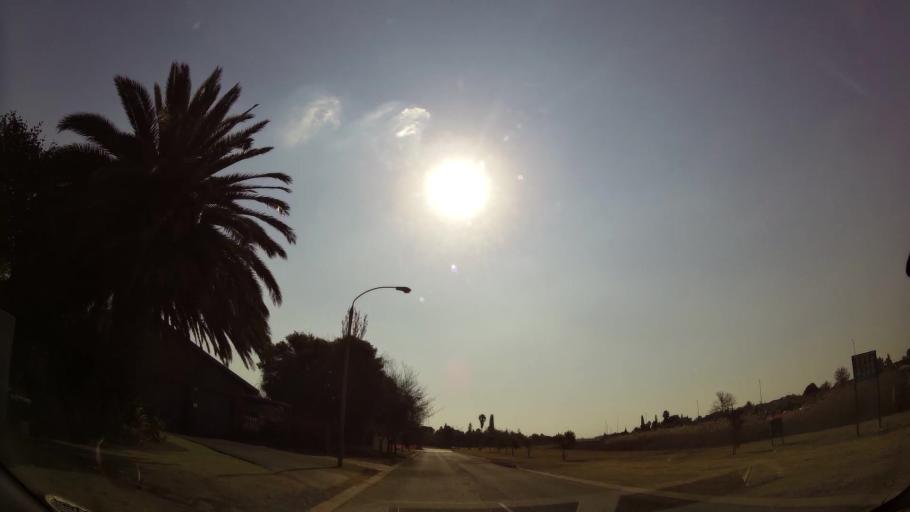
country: ZA
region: Gauteng
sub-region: Ekurhuleni Metropolitan Municipality
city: Benoni
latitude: -26.1481
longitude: 28.2868
